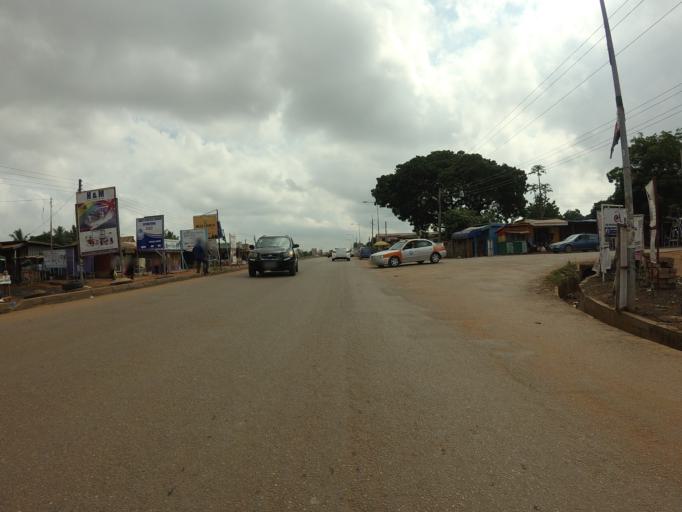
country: GH
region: Greater Accra
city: Teshi Old Town
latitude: 5.6078
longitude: -0.1117
